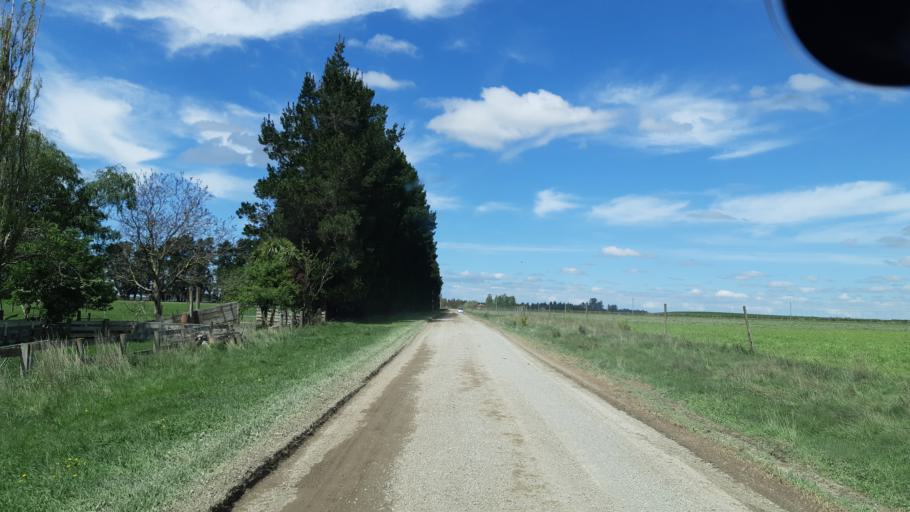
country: NZ
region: Canterbury
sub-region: Ashburton District
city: Methven
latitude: -43.6924
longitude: 171.4545
